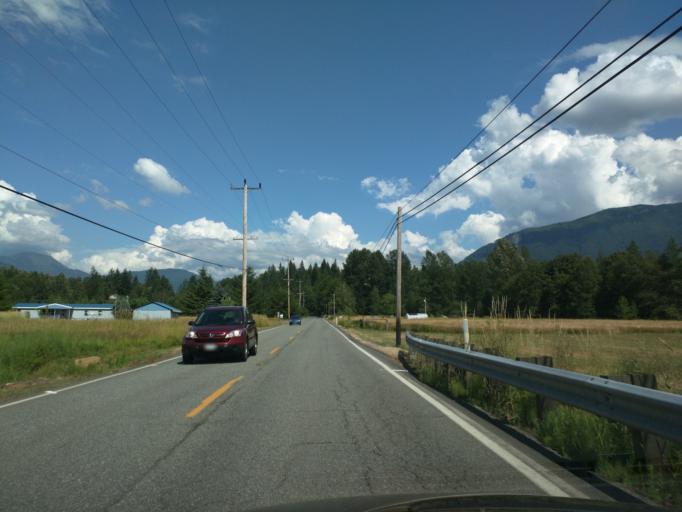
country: US
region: Washington
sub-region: Whatcom County
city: Peaceful Valley
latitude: 48.9170
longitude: -122.1088
